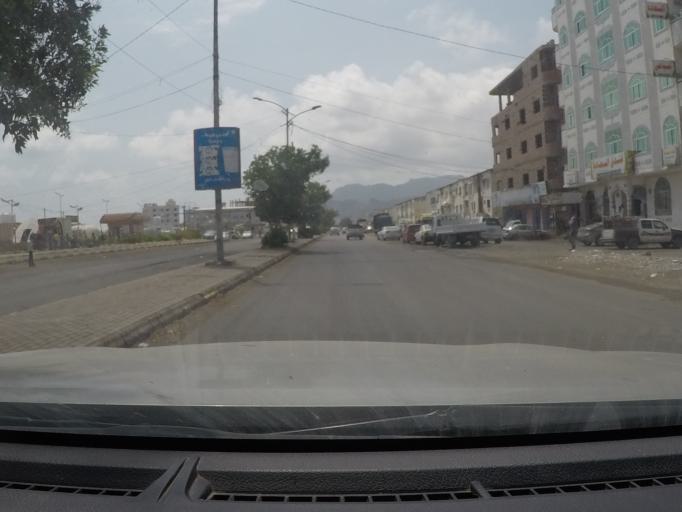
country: YE
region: Aden
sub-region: Khur Maksar
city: Khawr Maksar
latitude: 12.8173
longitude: 45.0428
